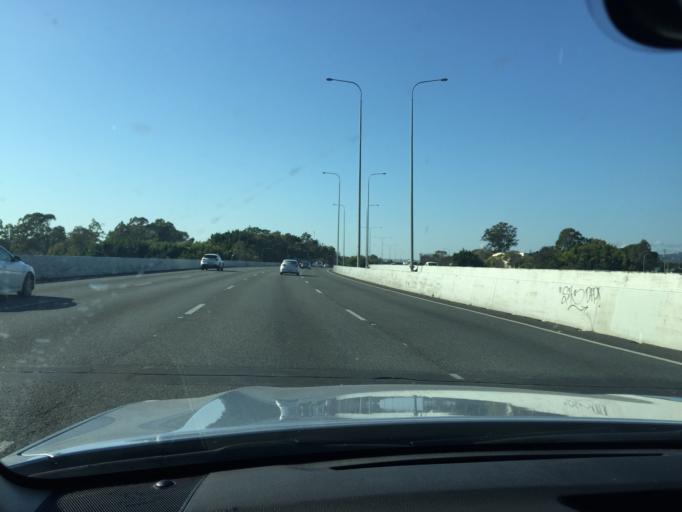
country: AU
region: Queensland
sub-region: Logan
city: Beenleigh
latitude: -27.7051
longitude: 153.2028
